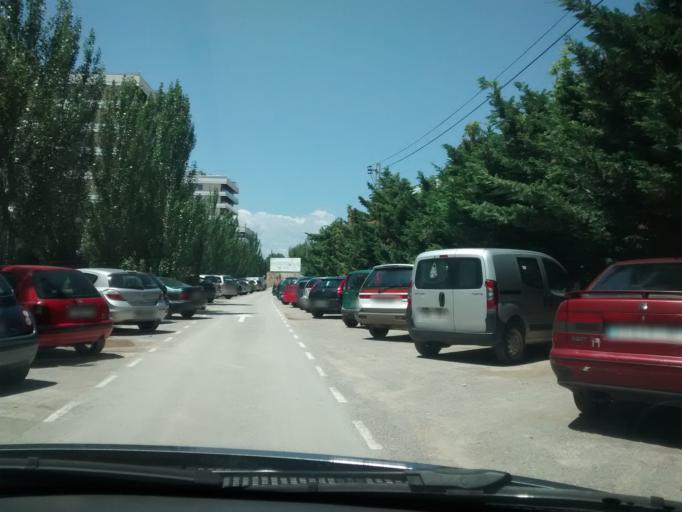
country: ES
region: Catalonia
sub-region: Provincia de Barcelona
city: Sant Joan Despi
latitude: 41.3583
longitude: 2.0686
